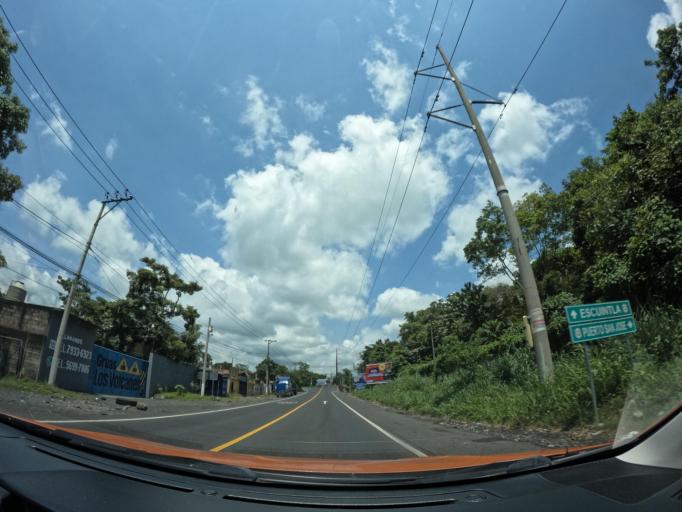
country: GT
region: Escuintla
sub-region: Municipio de Escuintla
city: Escuintla
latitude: 14.2800
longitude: -90.7888
